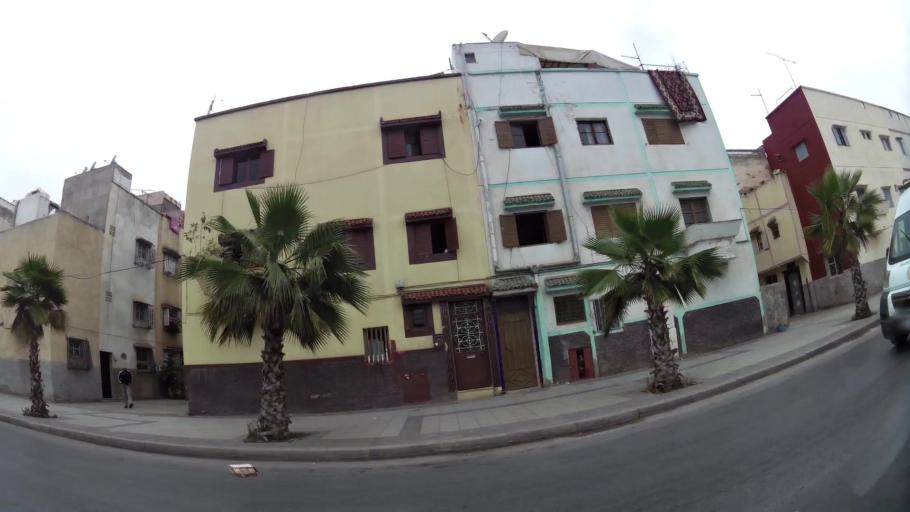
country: MA
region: Rabat-Sale-Zemmour-Zaer
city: Sale
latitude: 34.0458
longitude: -6.7975
